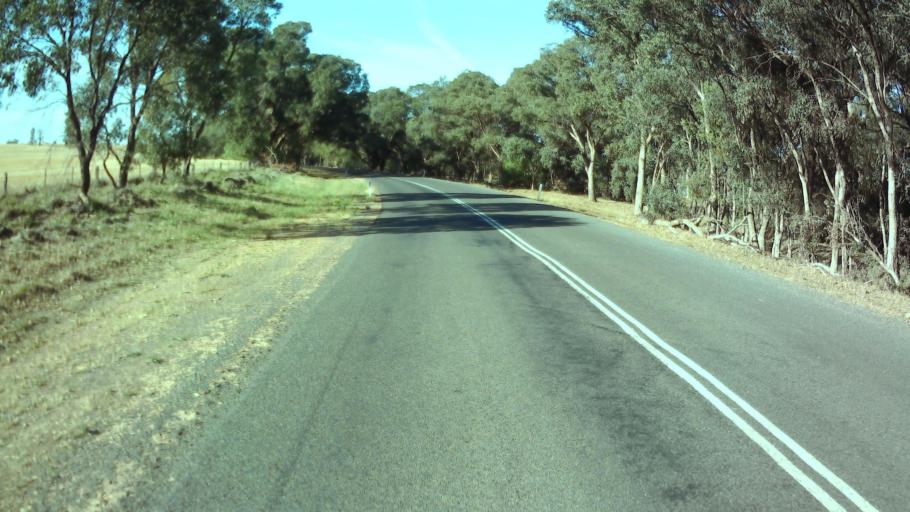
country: AU
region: New South Wales
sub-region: Weddin
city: Grenfell
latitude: -33.9941
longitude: 148.1331
